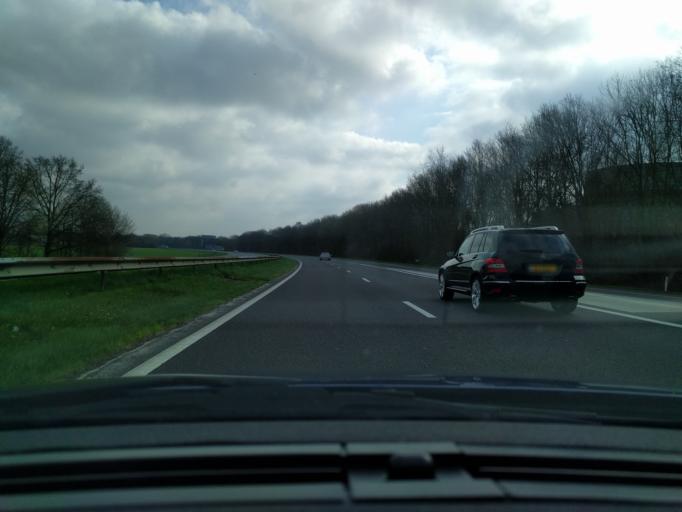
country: NL
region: Gelderland
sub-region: Gemeente Wijchen
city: Wijchen
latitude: 51.8129
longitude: 5.6991
